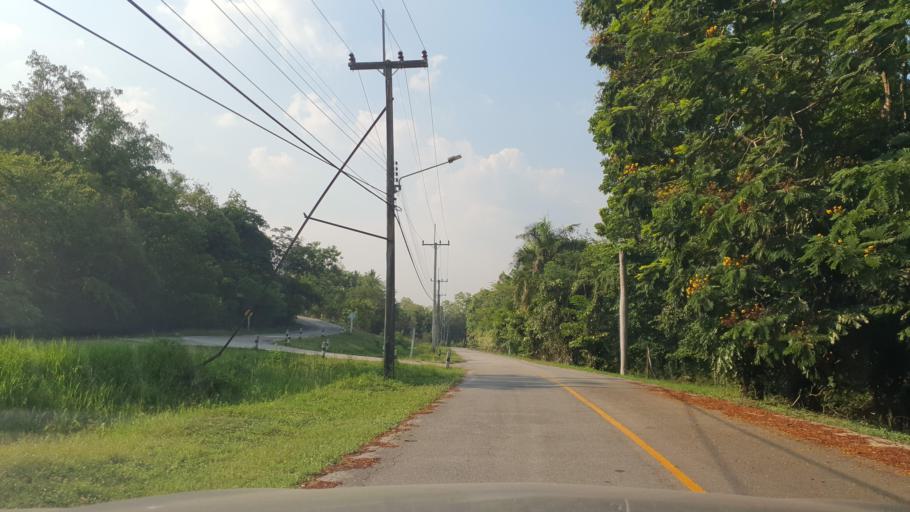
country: TH
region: Kanchanaburi
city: Sai Yok
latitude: 14.2275
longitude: 99.2313
